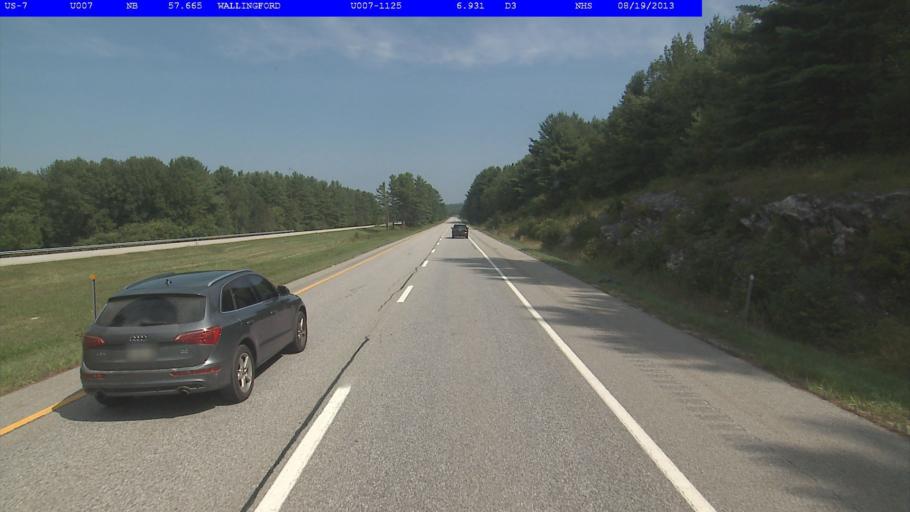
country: US
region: Vermont
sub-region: Rutland County
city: Rutland
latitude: 43.4917
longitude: -72.9697
